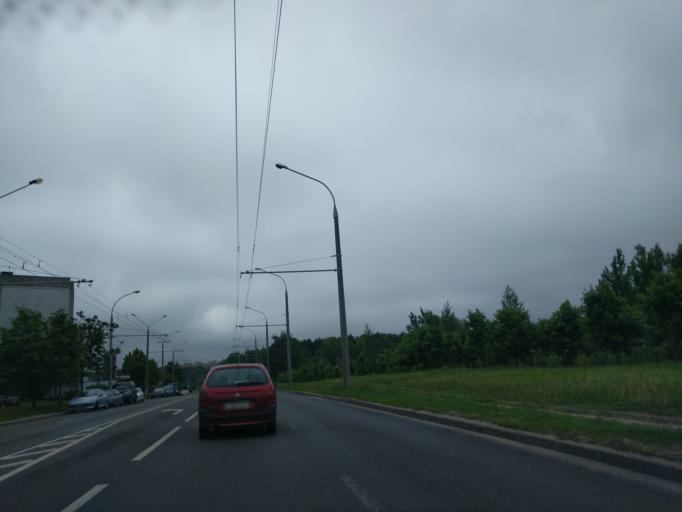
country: BY
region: Minsk
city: Novoye Medvezhino
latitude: 53.8900
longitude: 27.4408
